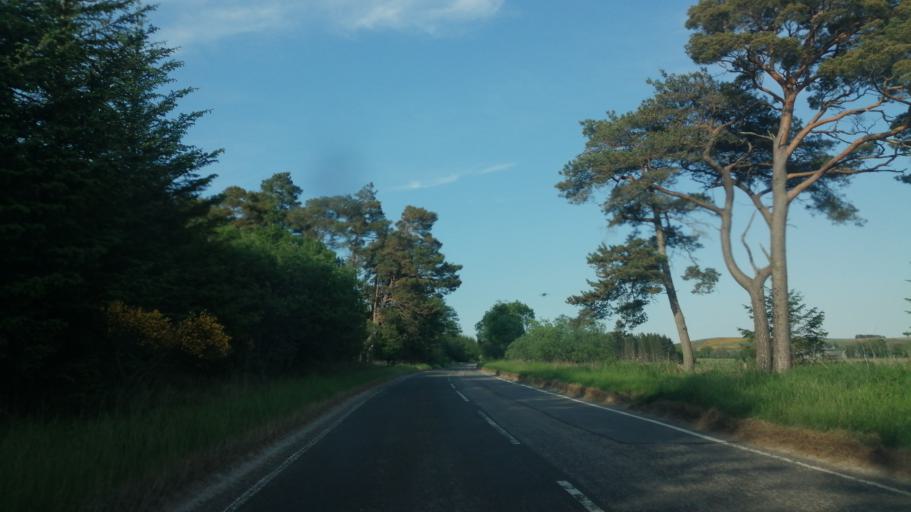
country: GB
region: Scotland
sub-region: Aberdeenshire
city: Huntly
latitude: 57.5700
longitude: -2.7799
